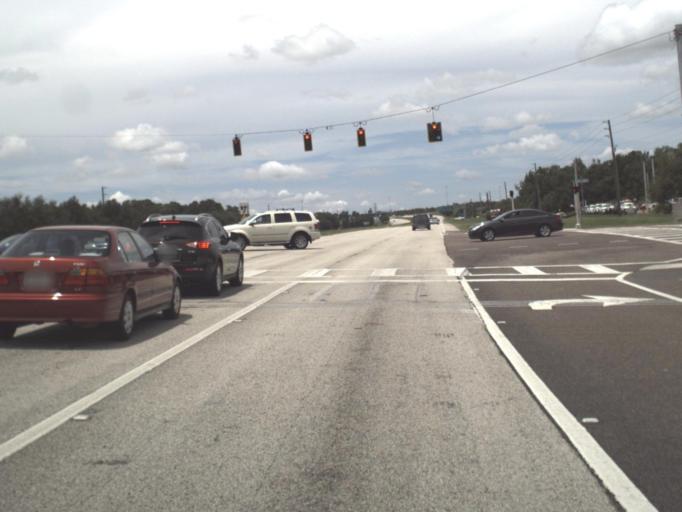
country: US
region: Florida
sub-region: Hillsborough County
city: Pebble Creek
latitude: 28.1871
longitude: -82.3741
